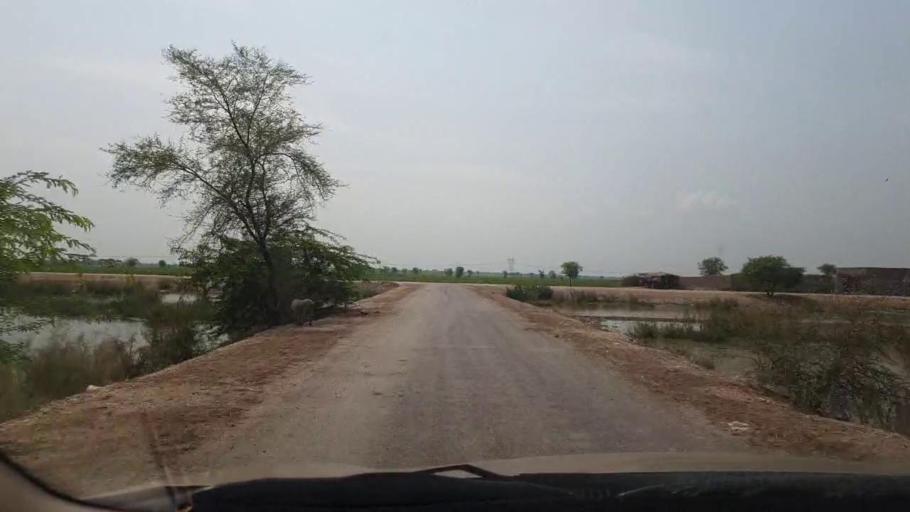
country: PK
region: Sindh
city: Goth Garelo
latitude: 27.4974
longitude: 68.1179
